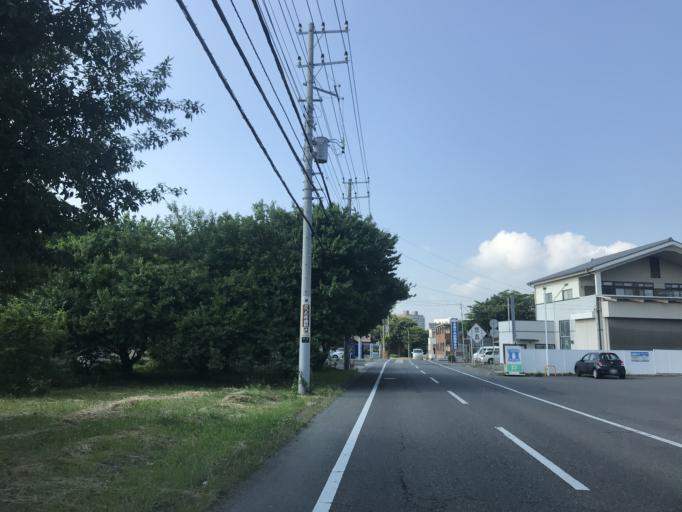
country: JP
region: Ibaraki
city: Naka
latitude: 36.0833
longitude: 140.1016
